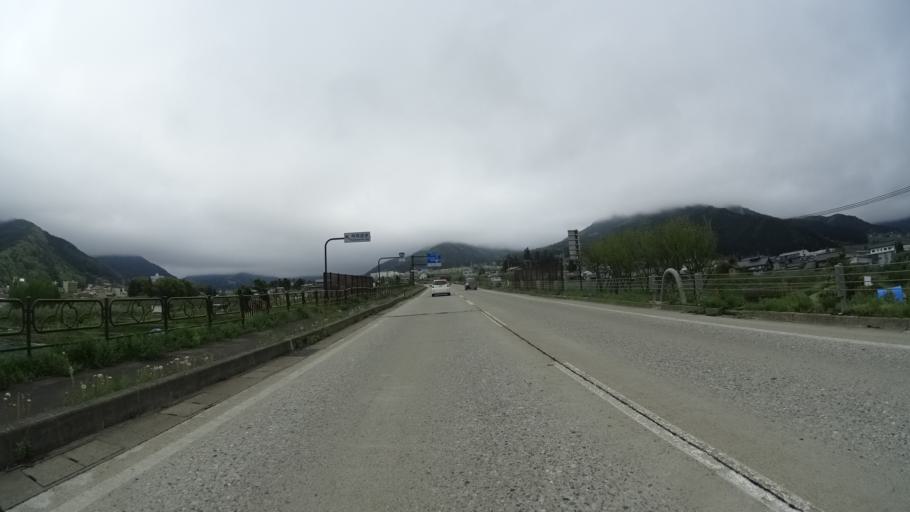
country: JP
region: Nagano
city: Nakano
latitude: 36.7377
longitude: 138.4099
